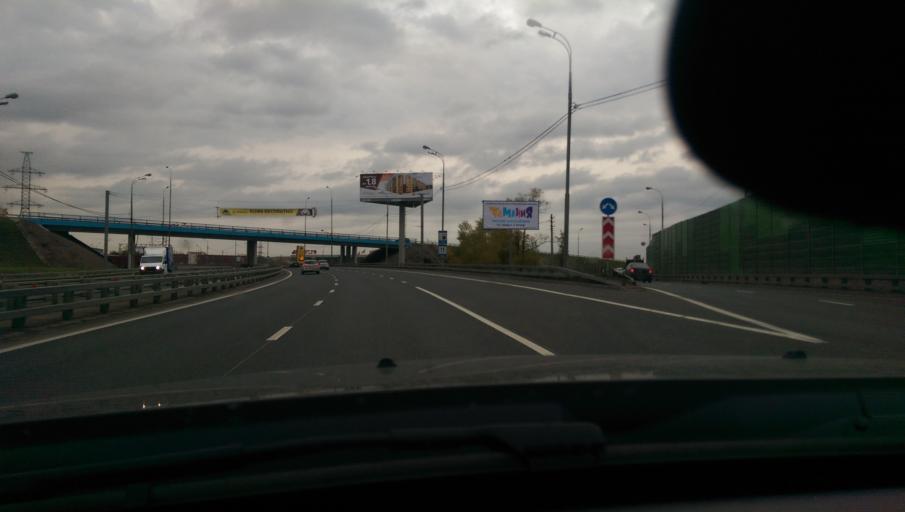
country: RU
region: Moscow
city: Vatutino
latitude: 55.9105
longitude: 37.6706
